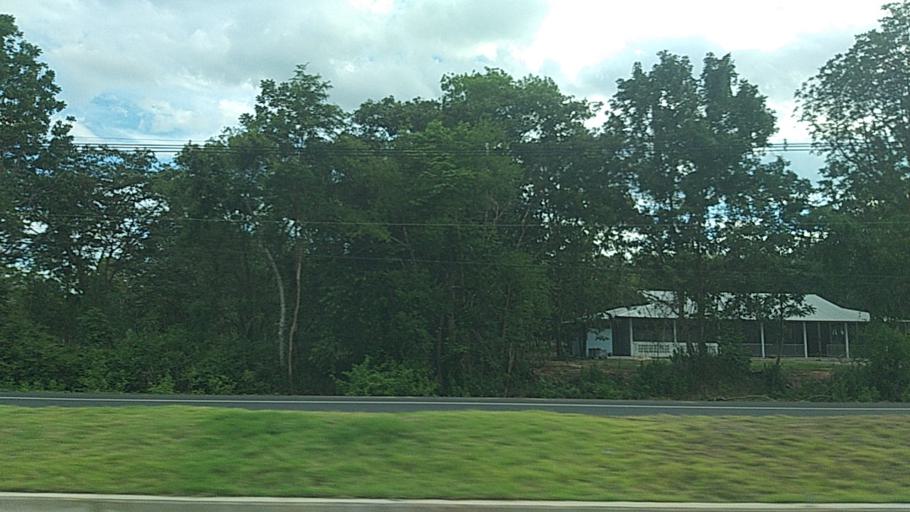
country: TH
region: Surin
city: Kap Choeng
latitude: 14.5565
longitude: 103.5034
